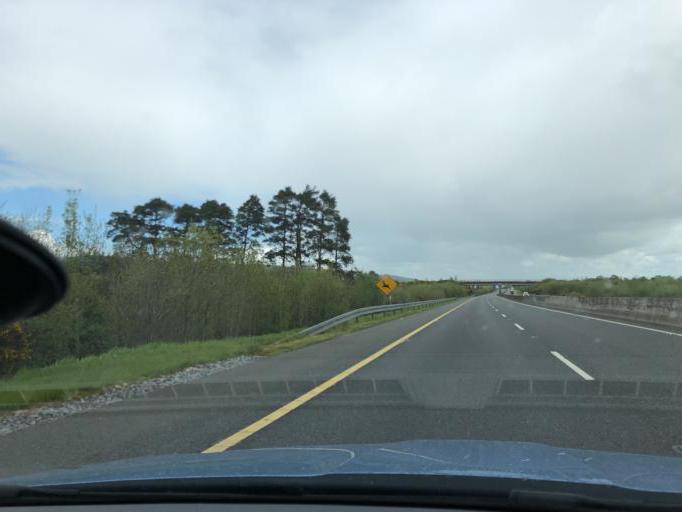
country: IE
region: Munster
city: Cahir
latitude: 52.3376
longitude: -8.0258
